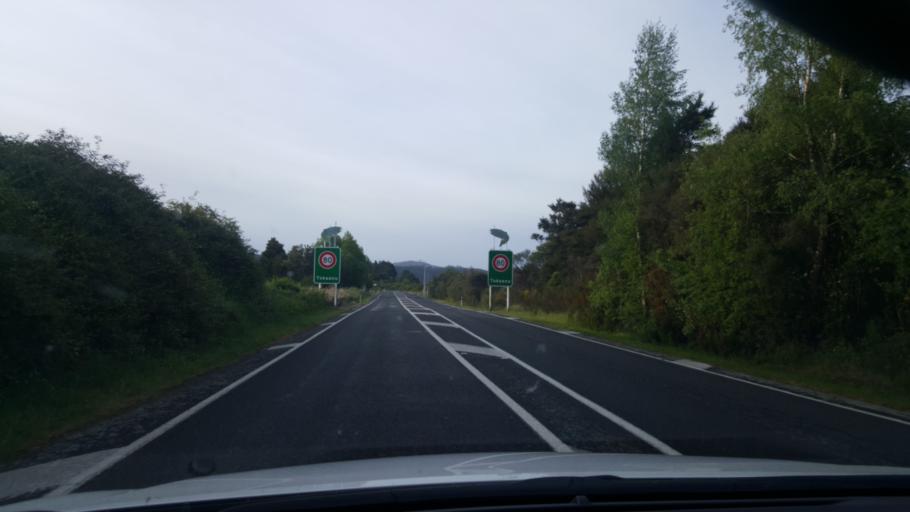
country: NZ
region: Waikato
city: Turangi
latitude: -38.9662
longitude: 175.7672
